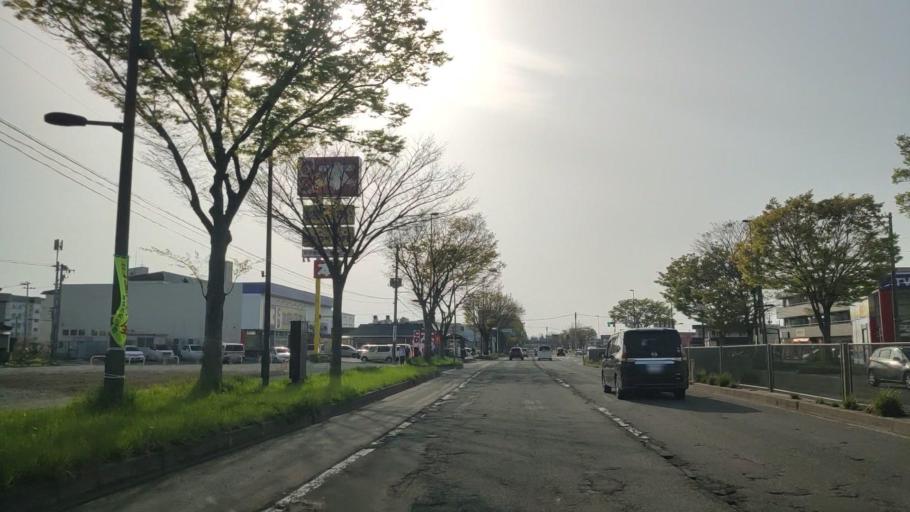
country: JP
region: Aomori
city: Aomori Shi
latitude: 40.8268
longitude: 140.7965
